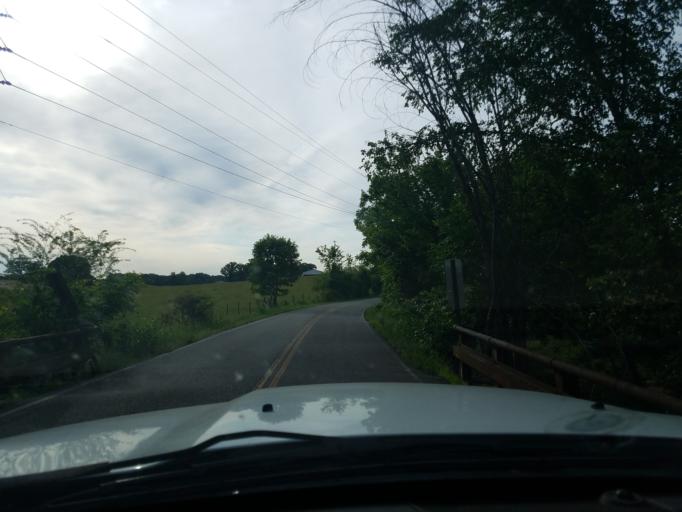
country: US
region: Tennessee
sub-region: Putnam County
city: Baxter
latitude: 36.1292
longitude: -85.5712
